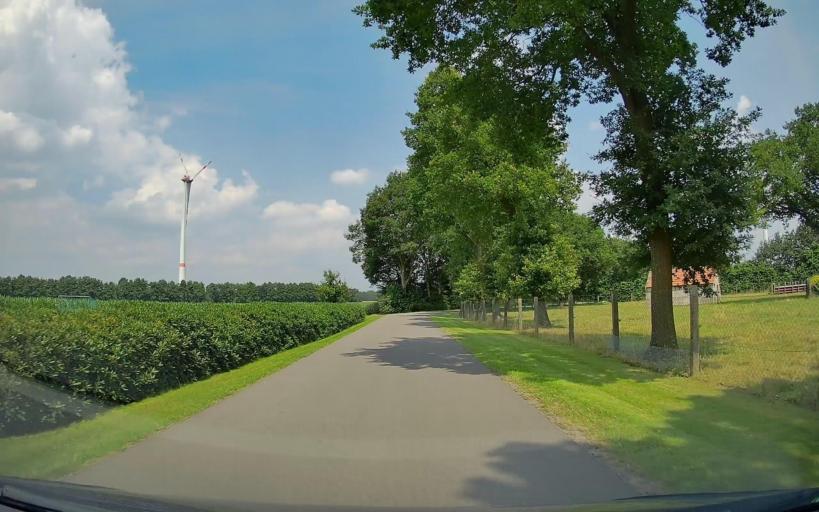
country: DE
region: Lower Saxony
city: Bosel
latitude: 53.0153
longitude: 7.9179
